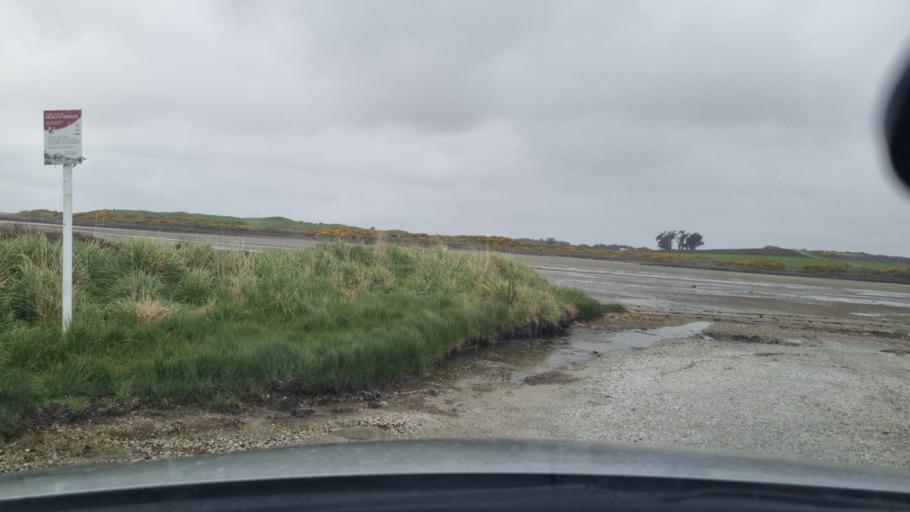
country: NZ
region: Southland
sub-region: Invercargill City
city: Bluff
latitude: -46.5202
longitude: 168.2824
